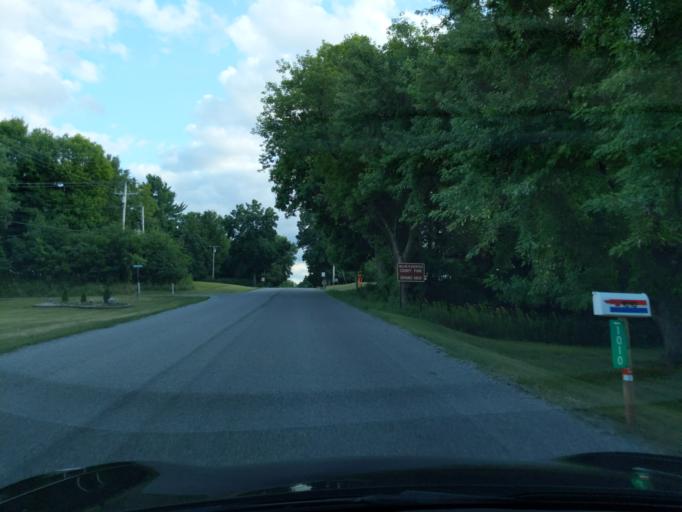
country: US
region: Michigan
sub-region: Ingham County
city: Holt
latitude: 42.6118
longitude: -84.5823
